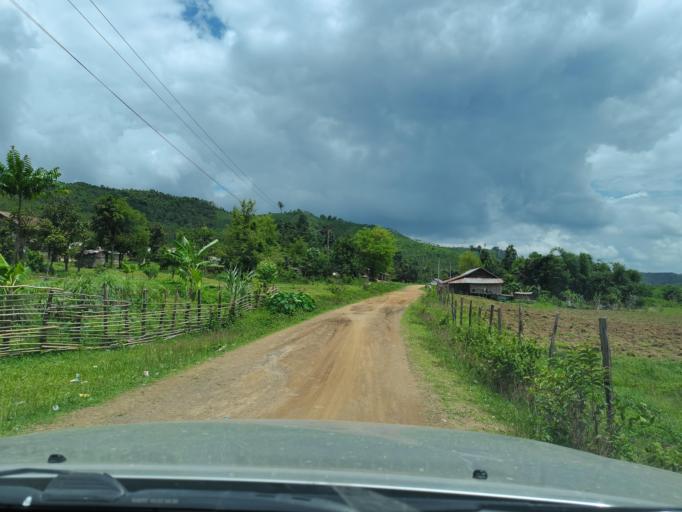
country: LA
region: Loungnamtha
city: Muang Long
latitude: 20.7254
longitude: 101.0142
